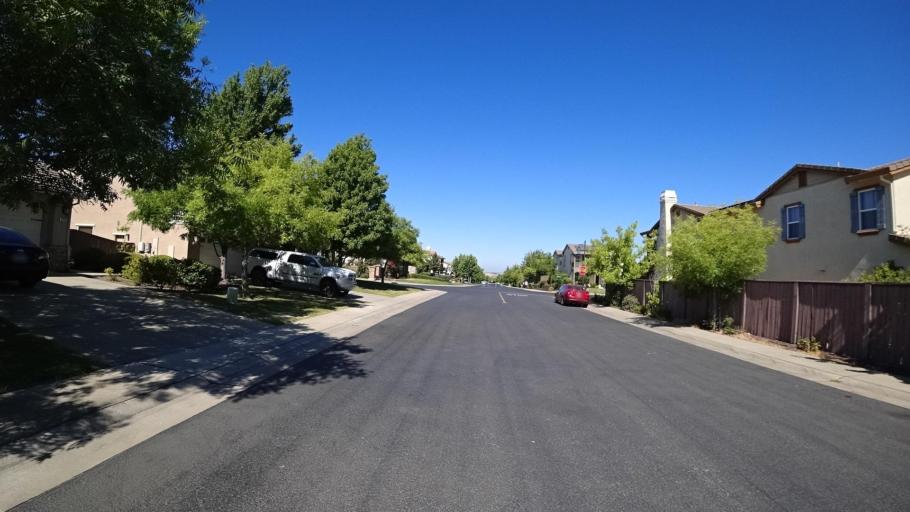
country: US
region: California
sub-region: Placer County
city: Rocklin
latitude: 38.8314
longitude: -121.2743
